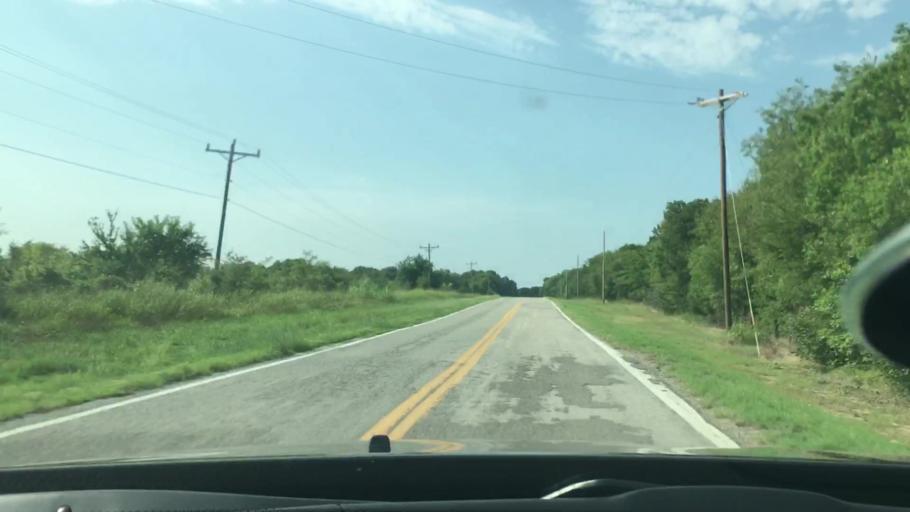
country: US
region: Oklahoma
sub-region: Johnston County
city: Tishomingo
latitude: 34.1767
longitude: -96.5838
